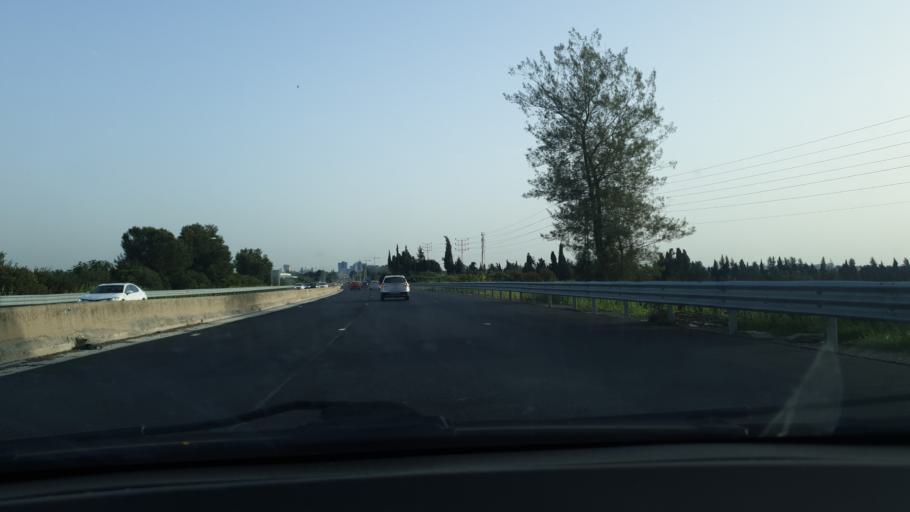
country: IL
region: Central District
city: Tel Mond
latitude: 32.2255
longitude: 34.8828
